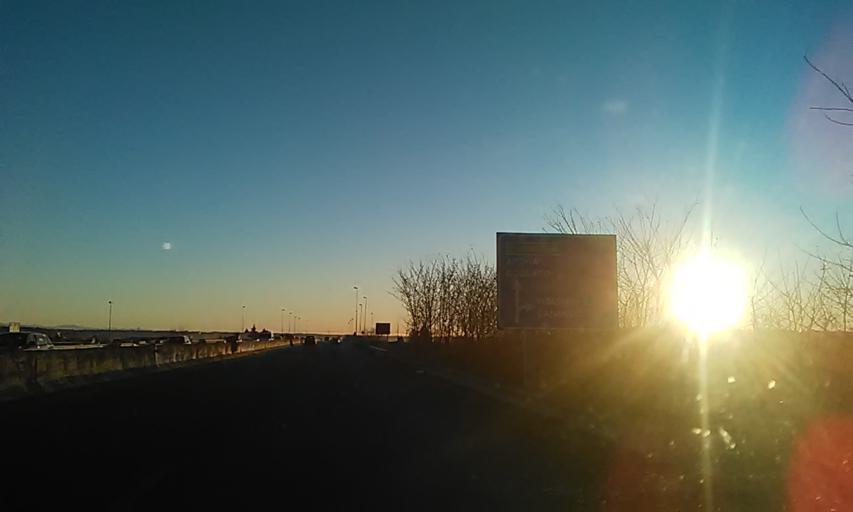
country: IT
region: Piedmont
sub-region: Provincia di Biella
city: Vigliano Biellese
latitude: 45.5555
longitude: 8.1102
